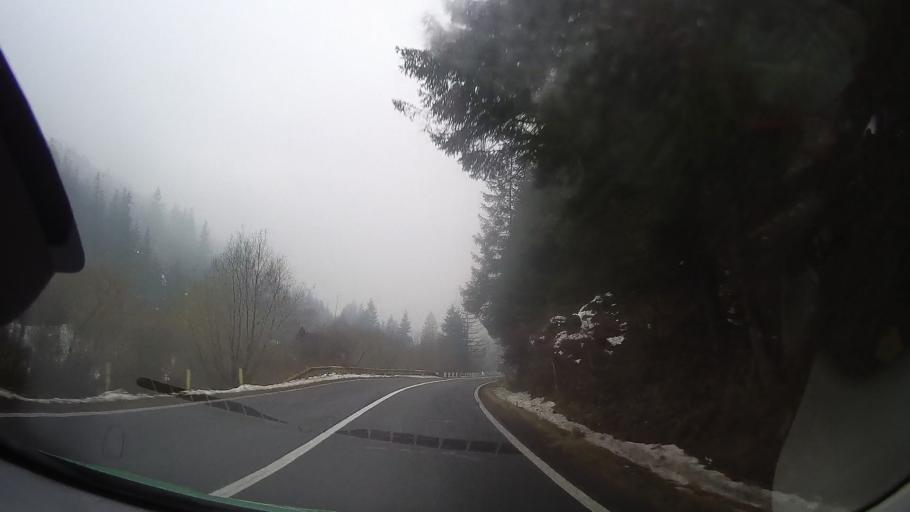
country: RO
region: Harghita
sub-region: Municipiul Gheorgheni
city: Gheorgheni
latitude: 46.7552
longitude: 25.6960
